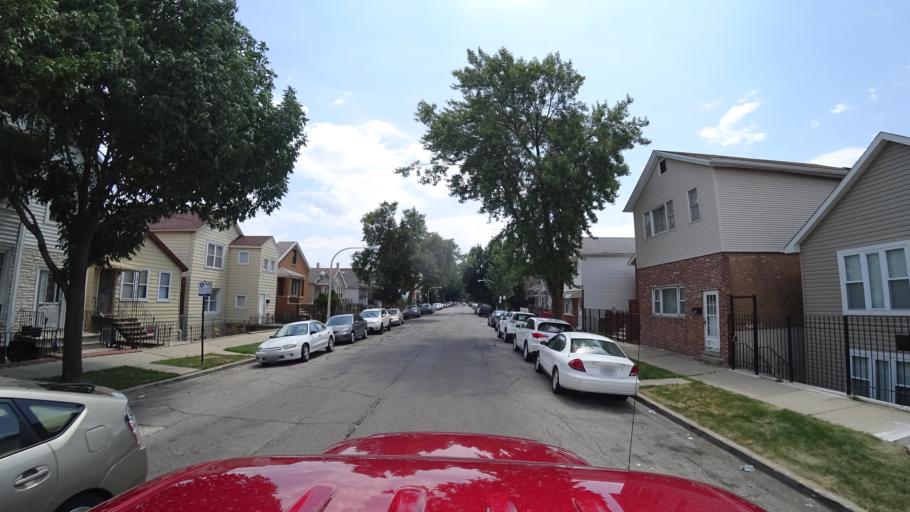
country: US
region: Illinois
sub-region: Cook County
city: Chicago
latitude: 41.8401
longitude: -87.6513
